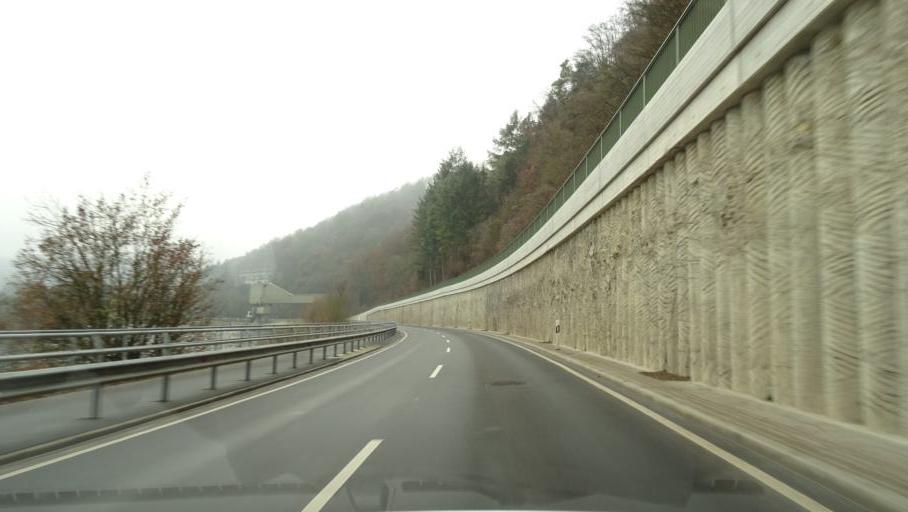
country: DE
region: Baden-Wuerttemberg
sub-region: Karlsruhe Region
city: Hassmersheim
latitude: 49.2930
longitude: 9.1297
